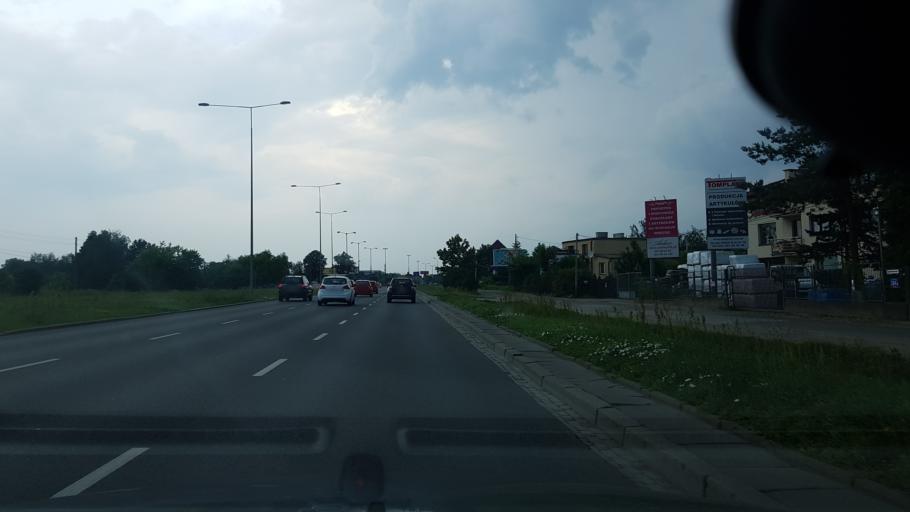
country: PL
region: Masovian Voivodeship
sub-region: Warszawa
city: Bialoleka
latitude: 52.3412
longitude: 20.9546
